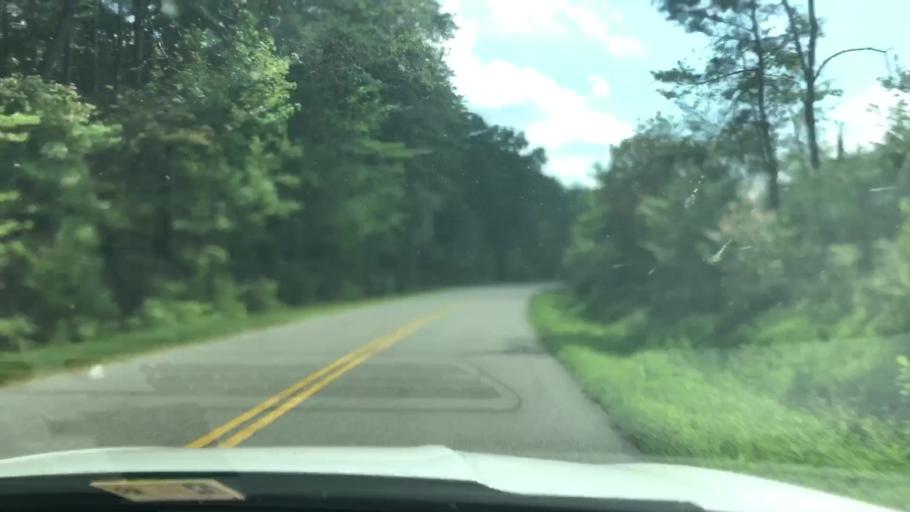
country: US
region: Virginia
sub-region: Middlesex County
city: Saluda
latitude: 37.6251
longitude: -76.7048
